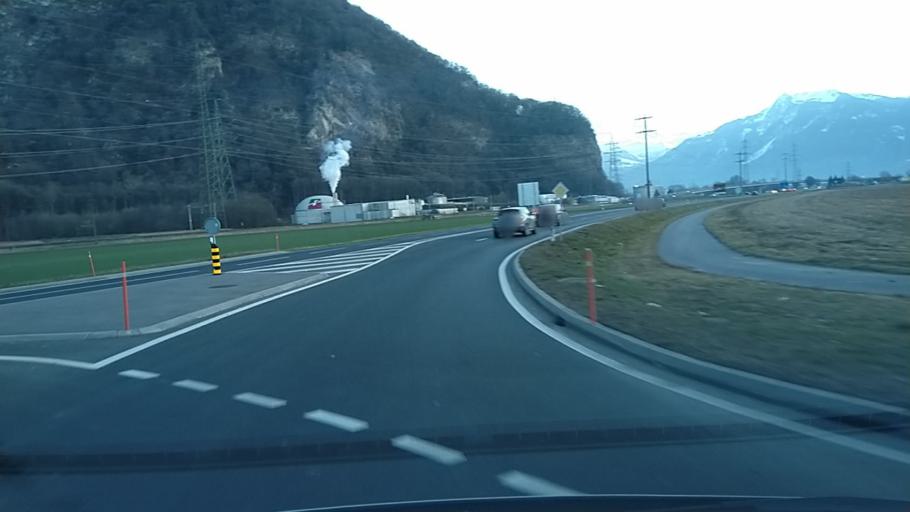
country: CH
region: Vaud
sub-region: Aigle District
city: Villeneuve
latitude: 46.3775
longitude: 6.9254
